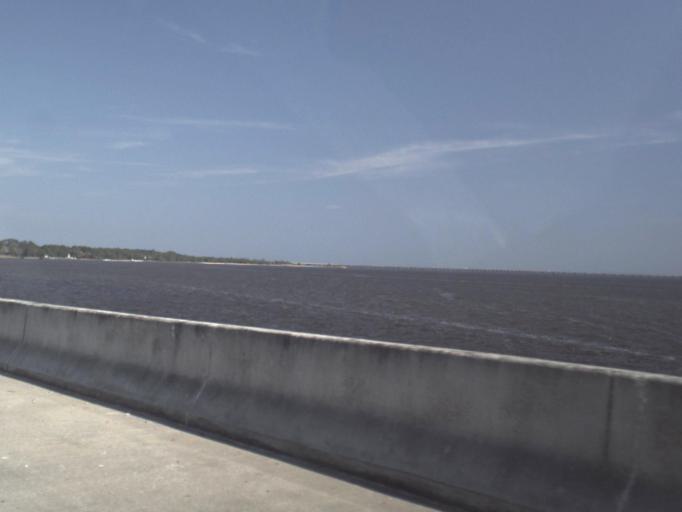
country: US
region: Florida
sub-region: Franklin County
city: Eastpoint
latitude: 29.7333
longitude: -84.9157
